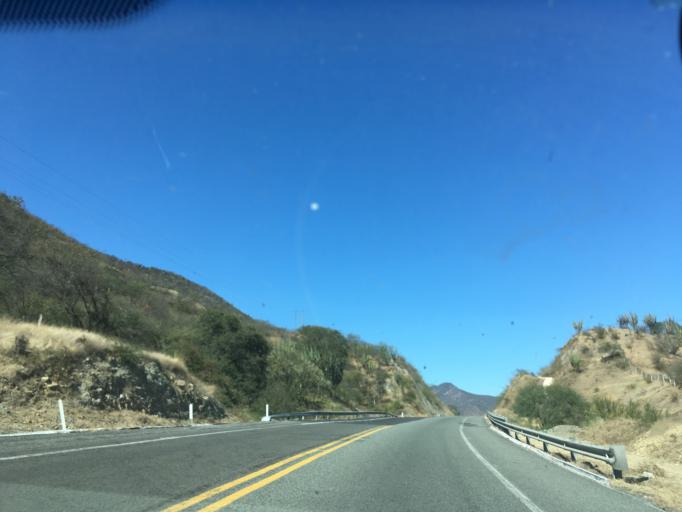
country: MX
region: Michoacan
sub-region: Arteaga
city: Infiernillo (Morelos de Infiernillo)
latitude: 18.3815
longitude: -101.8955
